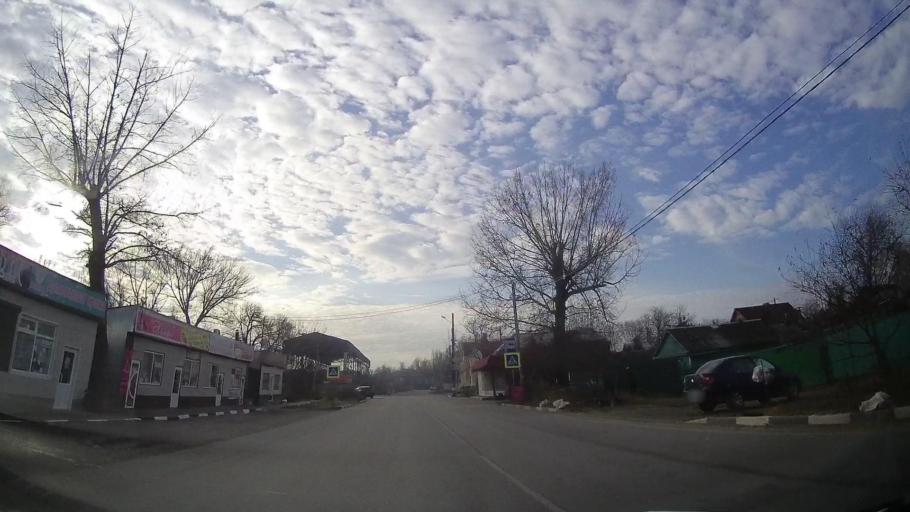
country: RU
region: Rostov
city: Bataysk
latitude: 47.1212
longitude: 39.7661
